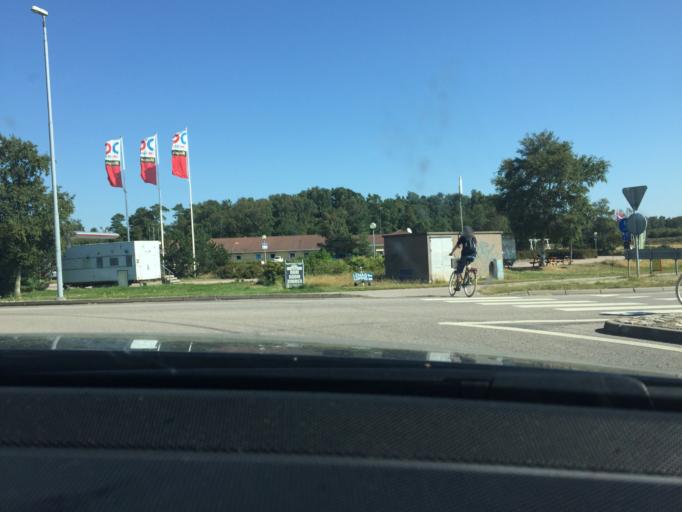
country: SE
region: Halland
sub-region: Laholms Kommun
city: Mellbystrand
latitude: 56.5044
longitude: 12.9554
